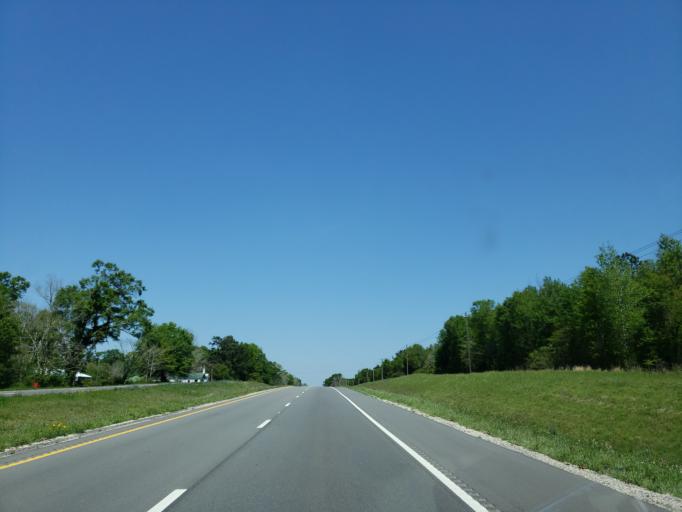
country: US
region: Mississippi
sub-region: Stone County
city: Wiggins
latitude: 30.8889
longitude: -89.1650
